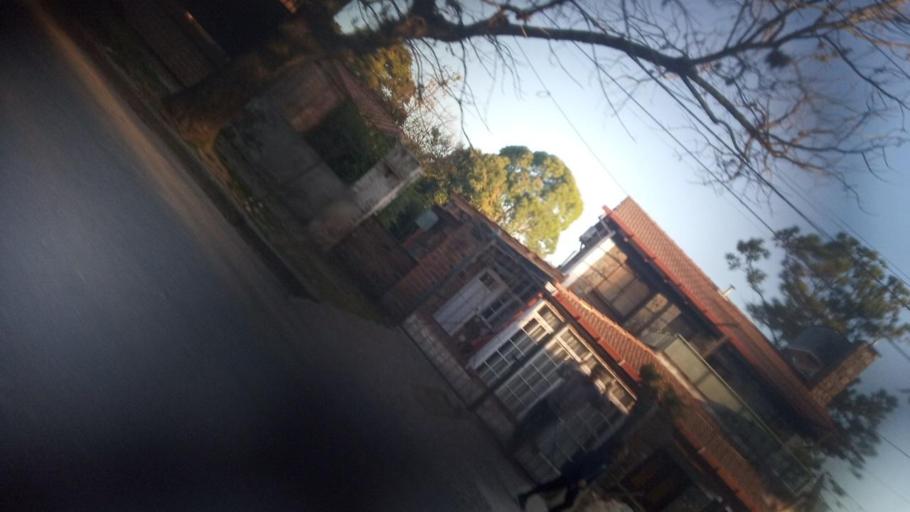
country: AR
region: Jujuy
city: San Salvador de Jujuy
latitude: -24.1696
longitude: -65.3198
